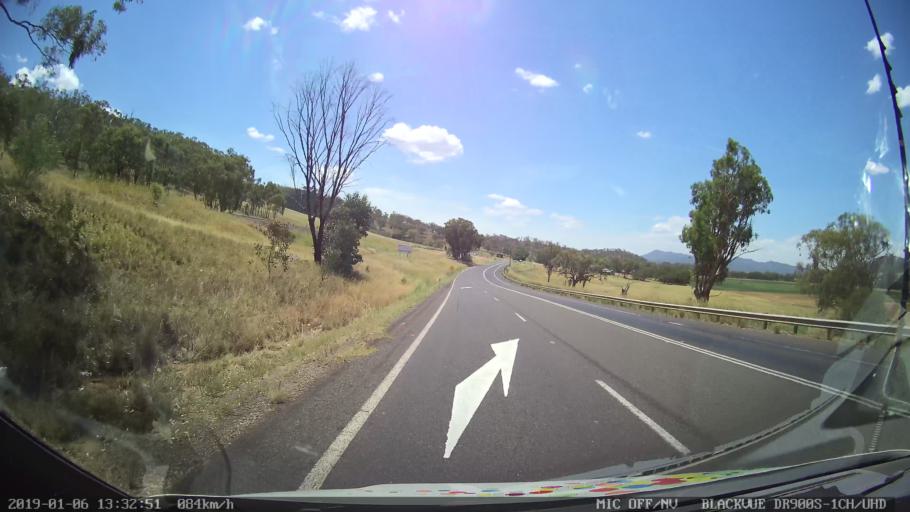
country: AU
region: New South Wales
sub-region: Tamworth Municipality
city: East Tamworth
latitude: -31.1059
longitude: 151.0015
